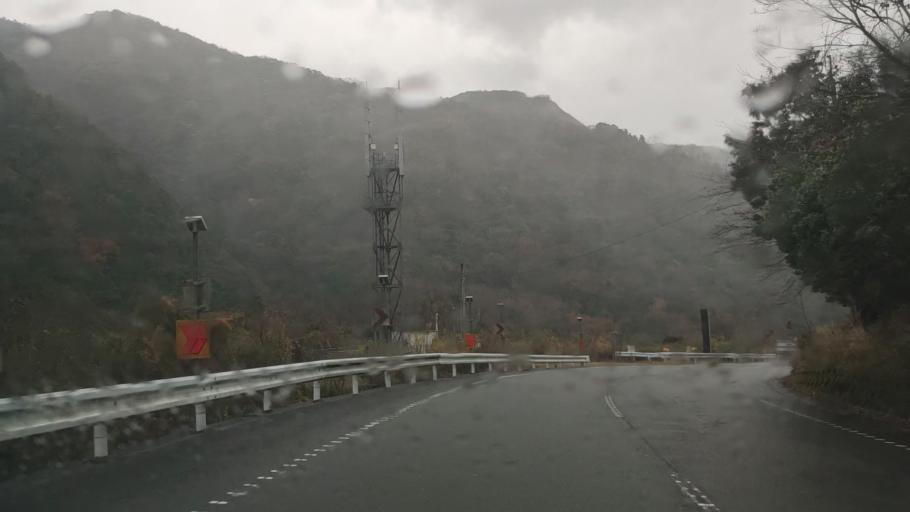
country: JP
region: Tokushima
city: Kamojimacho-jogejima
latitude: 34.1469
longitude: 134.3549
